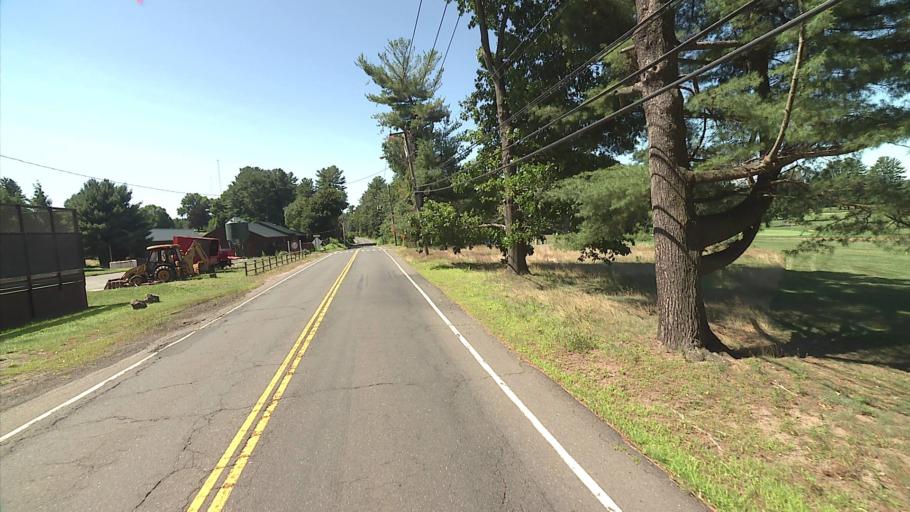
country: US
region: Connecticut
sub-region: Hartford County
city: Farmington
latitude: 41.7314
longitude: -72.8221
